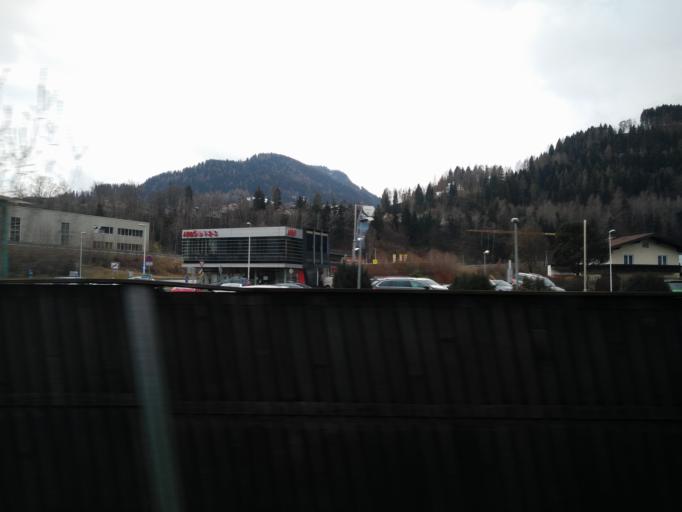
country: AT
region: Salzburg
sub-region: Politischer Bezirk Sankt Johann im Pongau
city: Bischofshofen
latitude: 47.4057
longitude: 13.2196
